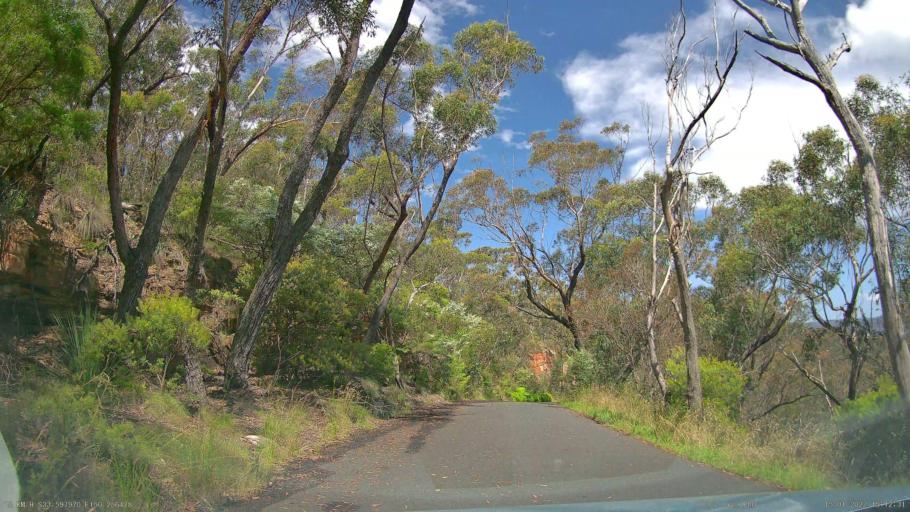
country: AU
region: New South Wales
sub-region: Blue Mountains Municipality
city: Blackheath
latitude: -33.5980
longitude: 150.2565
